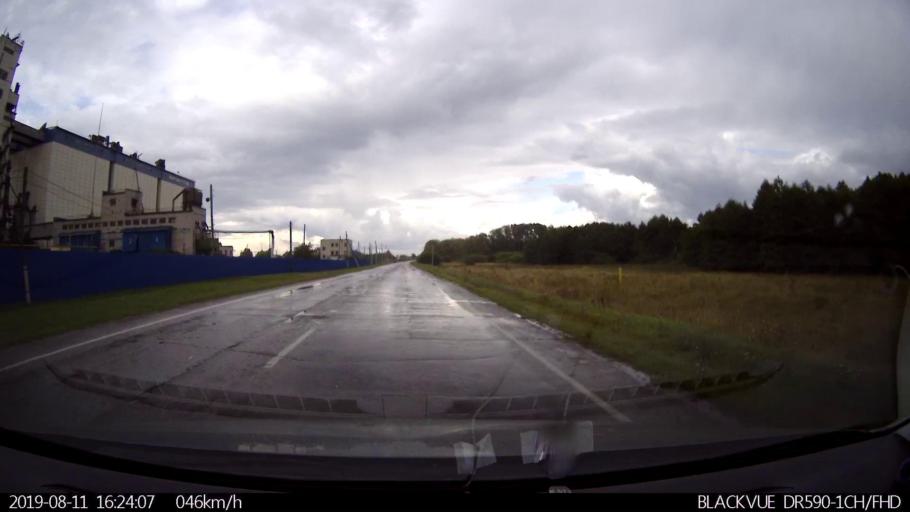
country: RU
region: Ulyanovsk
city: Mayna
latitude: 54.0987
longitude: 47.5916
